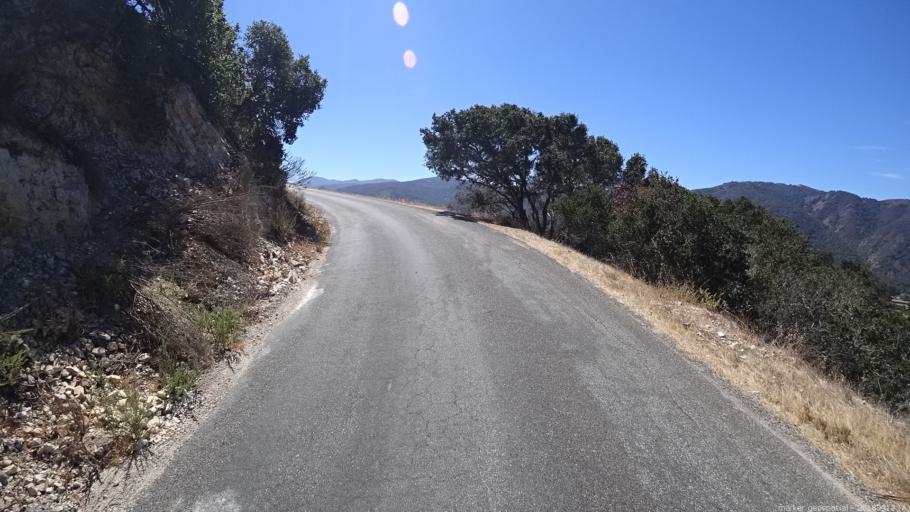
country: US
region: California
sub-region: Monterey County
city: Carmel Valley Village
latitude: 36.4844
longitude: -121.7236
